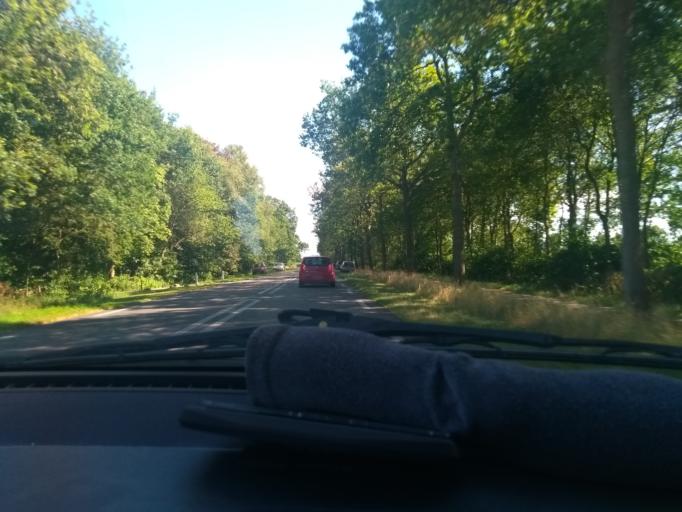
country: NL
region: Drenthe
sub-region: Gemeente Tynaarlo
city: Vries
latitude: 53.1320
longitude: 6.4996
